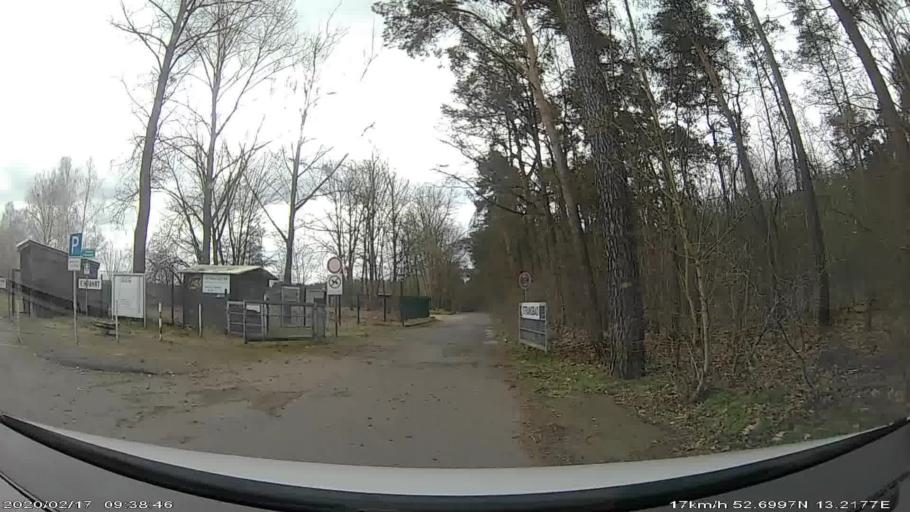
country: DE
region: Brandenburg
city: Leegebruch
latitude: 52.6997
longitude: 13.2178
